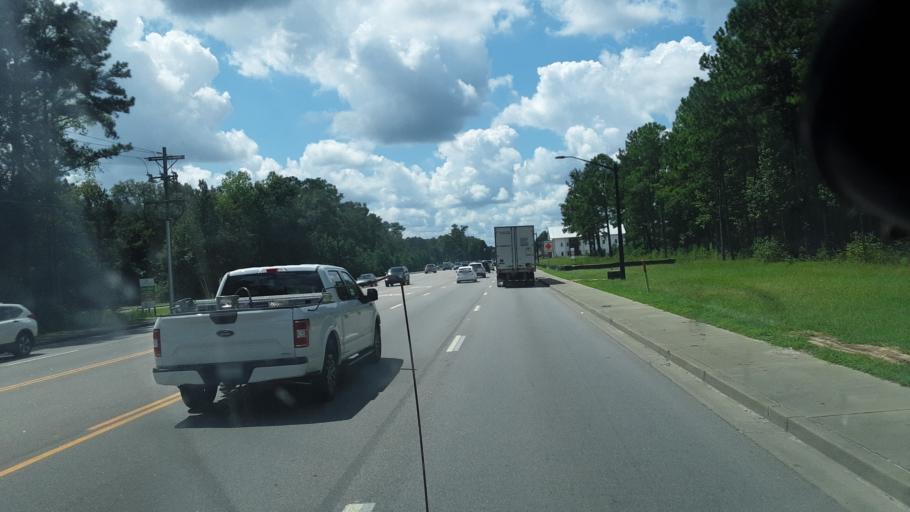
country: US
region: South Carolina
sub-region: Berkeley County
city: Sangaree
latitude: 33.0618
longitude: -80.0950
